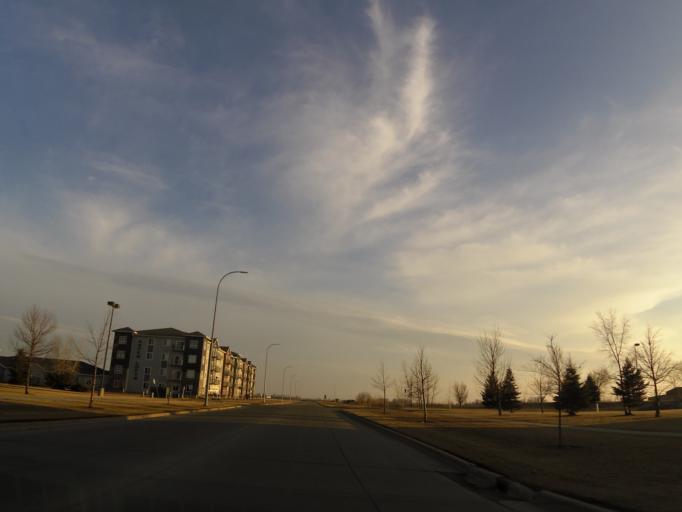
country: US
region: North Dakota
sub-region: Grand Forks County
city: Grand Forks
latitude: 47.8866
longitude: -97.0823
